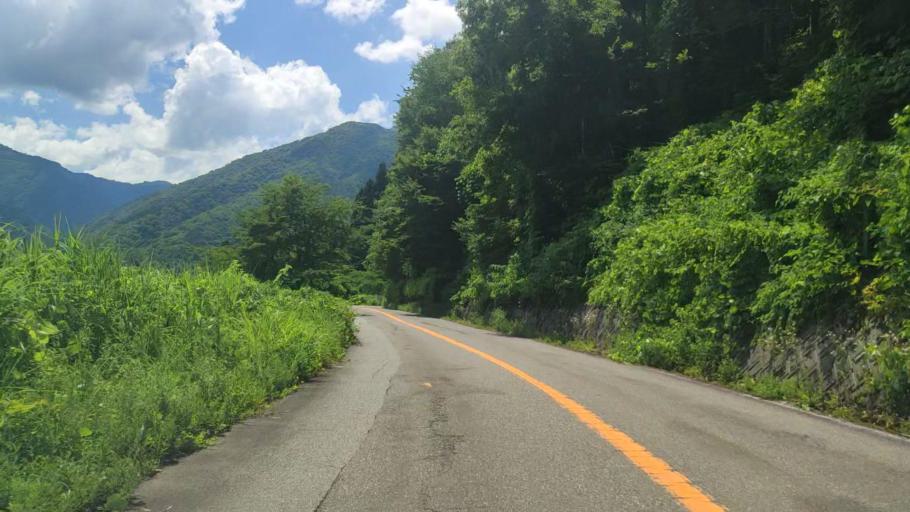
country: JP
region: Fukui
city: Ono
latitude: 35.9102
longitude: 136.5303
